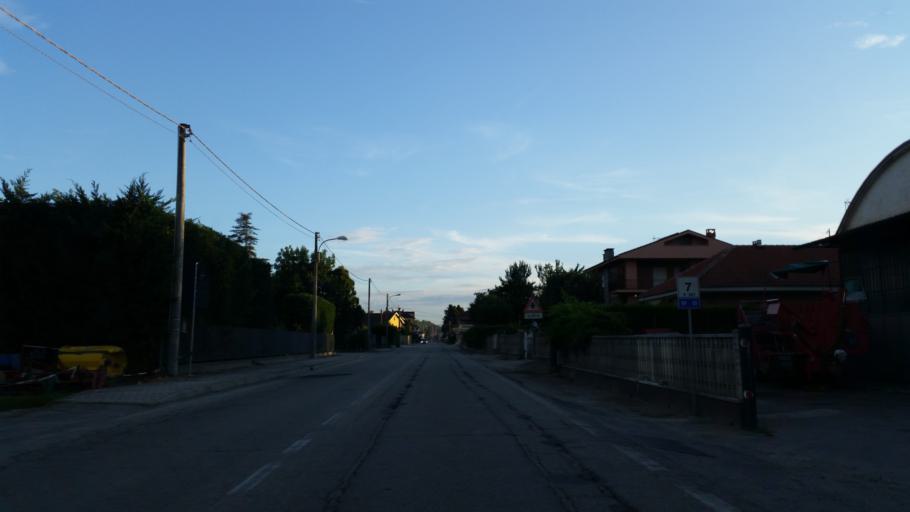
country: IT
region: Piedmont
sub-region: Provincia di Asti
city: Isola d'Asti
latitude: 44.8423
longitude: 8.1885
